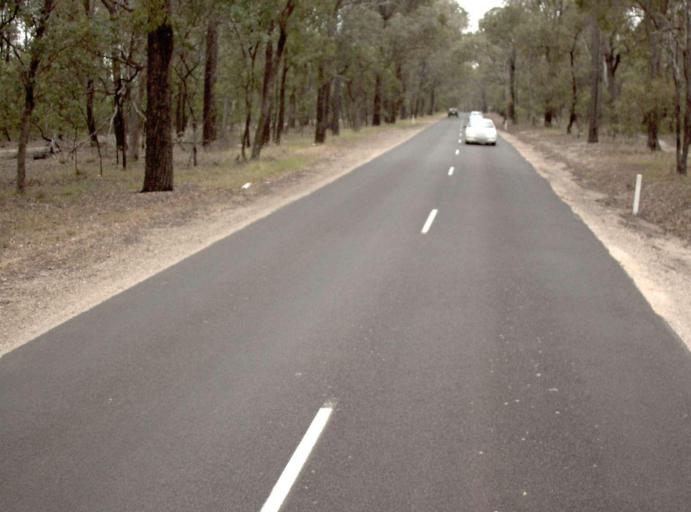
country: AU
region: Victoria
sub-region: Wellington
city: Heyfield
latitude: -37.9439
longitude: 146.7645
